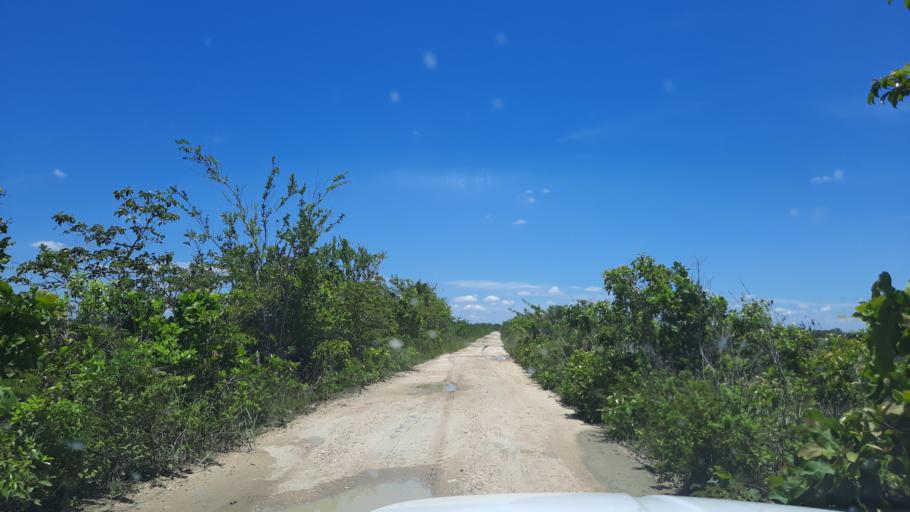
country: BZ
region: Cayo
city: Belmopan
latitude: 17.3810
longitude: -88.4917
